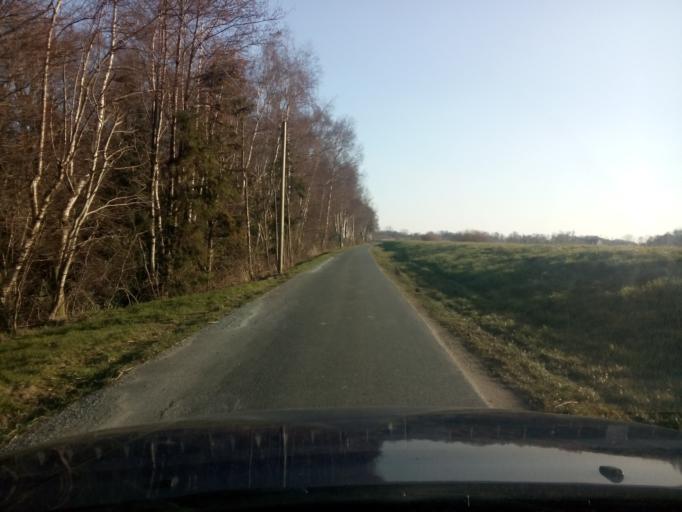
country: DE
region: Lower Saxony
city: Lilienthal
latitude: 53.1530
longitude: 8.8421
